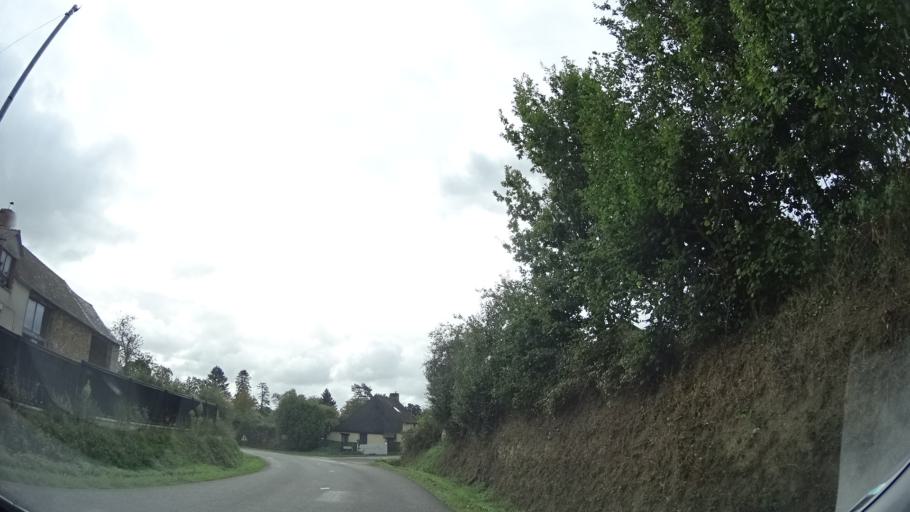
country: FR
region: Brittany
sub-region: Departement d'Ille-et-Vilaine
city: Montreuil-sur-Ille
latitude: 48.2969
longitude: -1.6422
